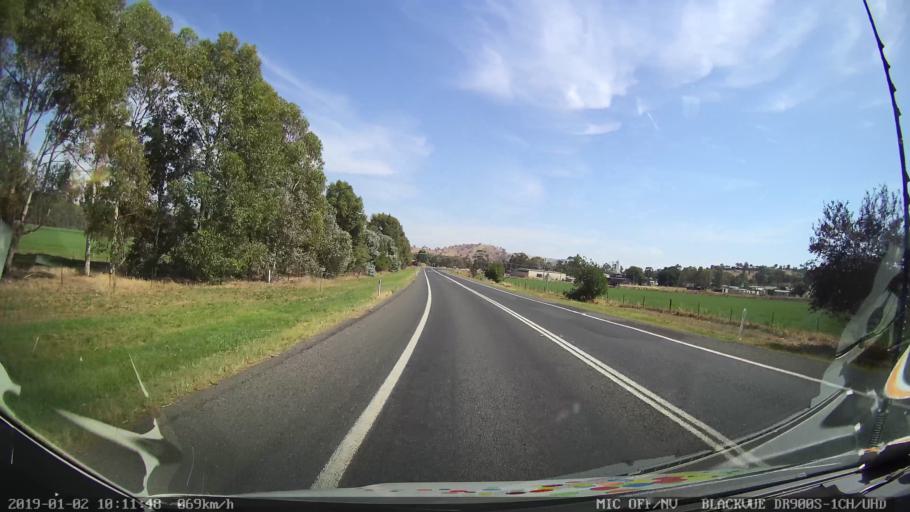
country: AU
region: New South Wales
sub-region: Gundagai
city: Gundagai
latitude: -35.0892
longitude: 148.0944
